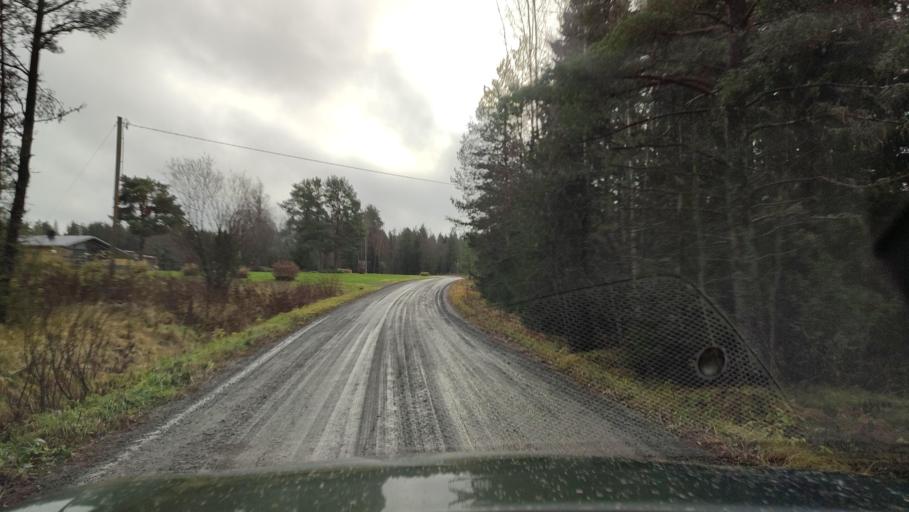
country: FI
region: Ostrobothnia
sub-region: Sydosterbotten
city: Naerpes
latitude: 62.4645
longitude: 21.4900
